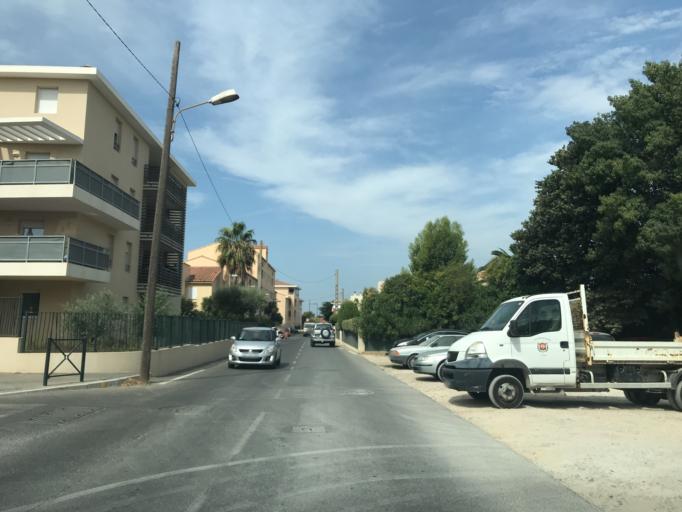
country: FR
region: Provence-Alpes-Cote d'Azur
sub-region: Departement du Var
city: Six-Fours-les-Plages
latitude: 43.0927
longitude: 5.8350
